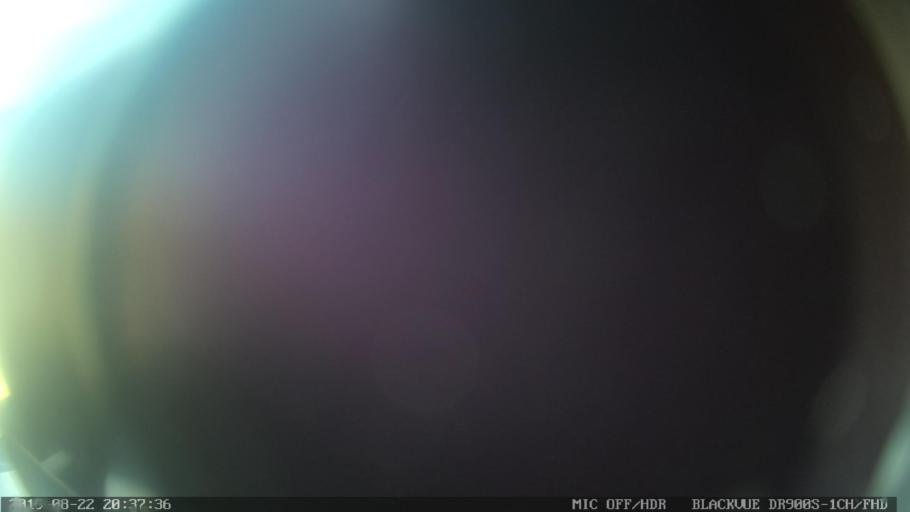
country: PT
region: Portalegre
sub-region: Nisa
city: Nisa
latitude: 39.6757
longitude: -7.7364
